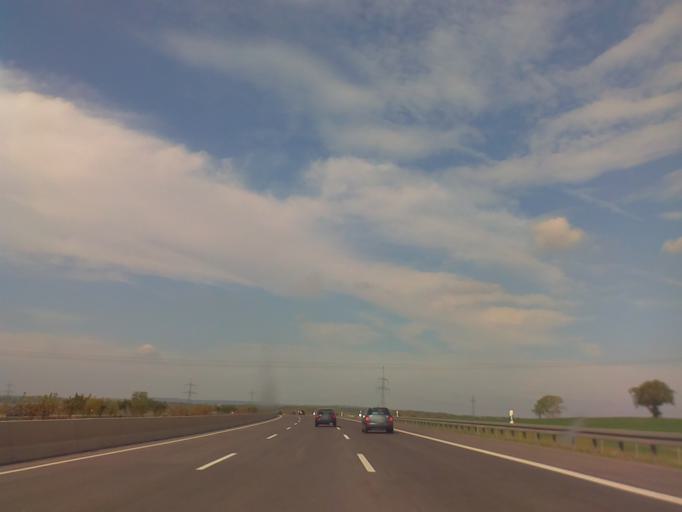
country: DE
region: Thuringia
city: Haina
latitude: 50.9664
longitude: 10.4891
